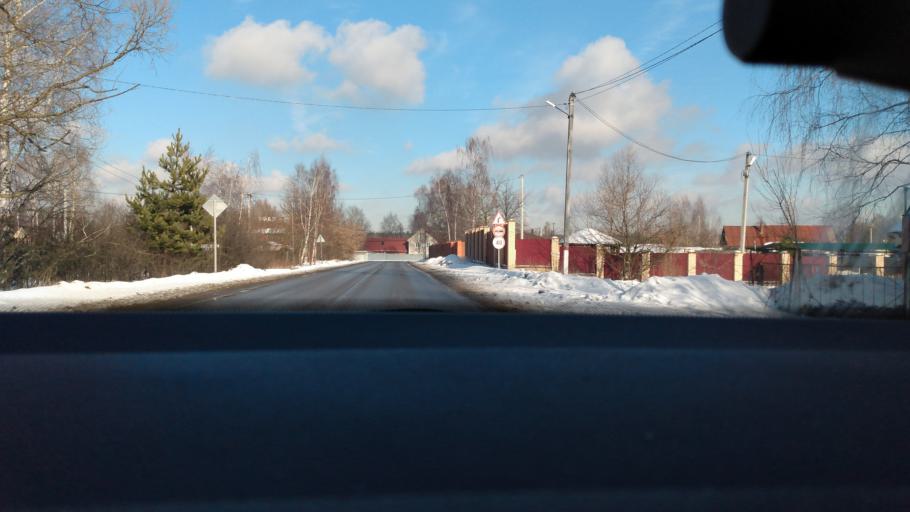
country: RU
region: Moskovskaya
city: Kratovo
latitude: 55.6374
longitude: 38.1652
